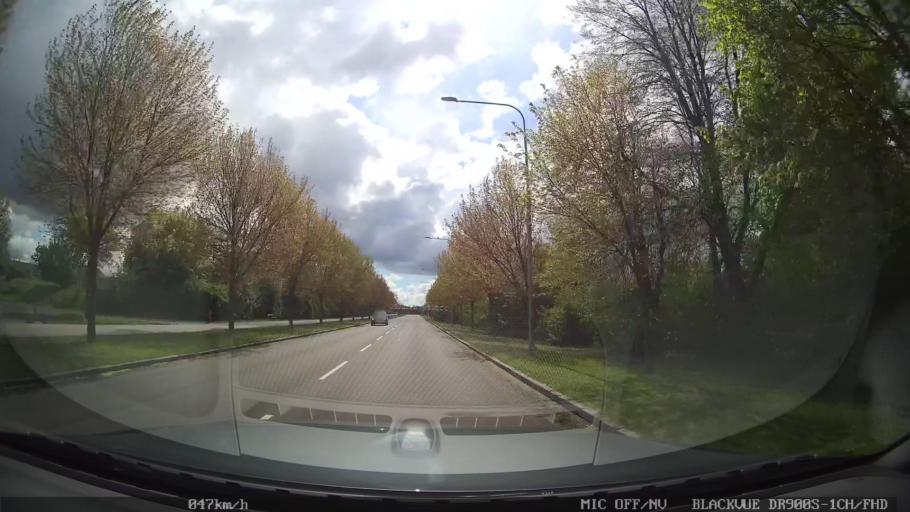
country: SE
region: Skane
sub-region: Landskrona
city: Landskrona
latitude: 55.8936
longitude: 12.8154
